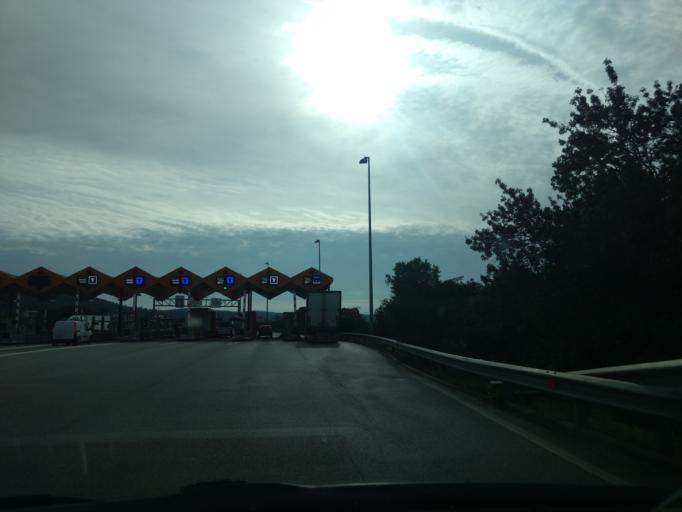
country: ES
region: Catalonia
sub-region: Provincia de Girona
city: la Jonquera
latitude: 42.4079
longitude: 2.8754
